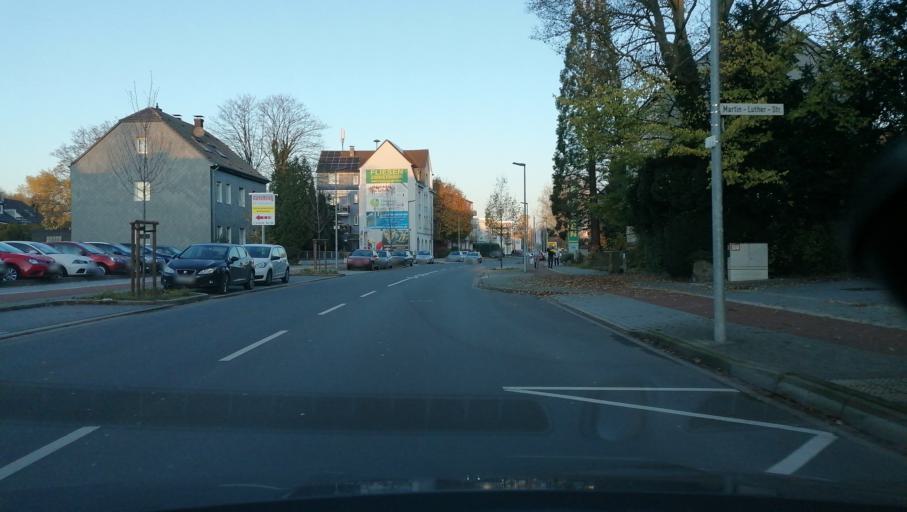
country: DE
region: North Rhine-Westphalia
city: Gevelsberg
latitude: 51.3246
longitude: 7.3506
